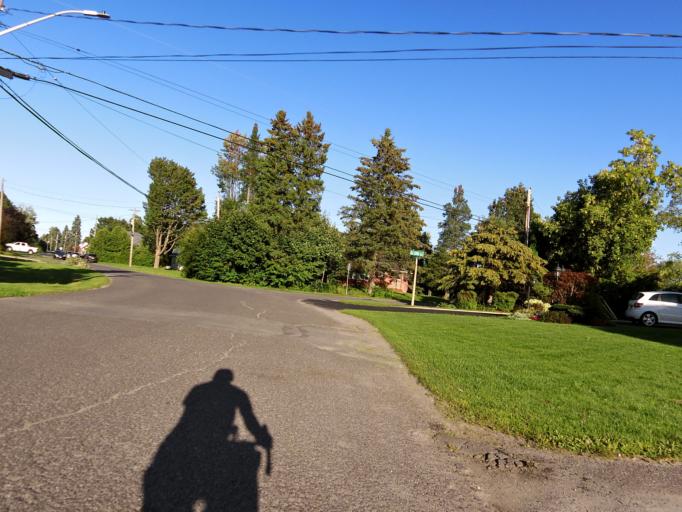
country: CA
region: Ontario
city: Ottawa
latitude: 45.3552
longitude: -75.7169
